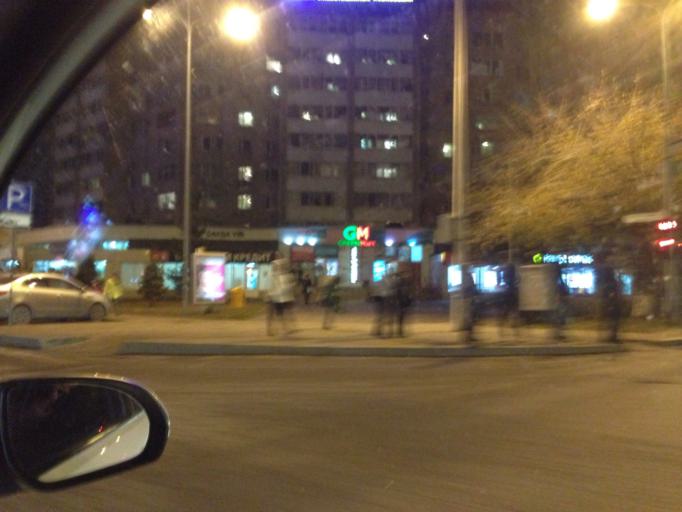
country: KZ
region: Astana Qalasy
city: Astana
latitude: 51.1714
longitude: 71.4258
